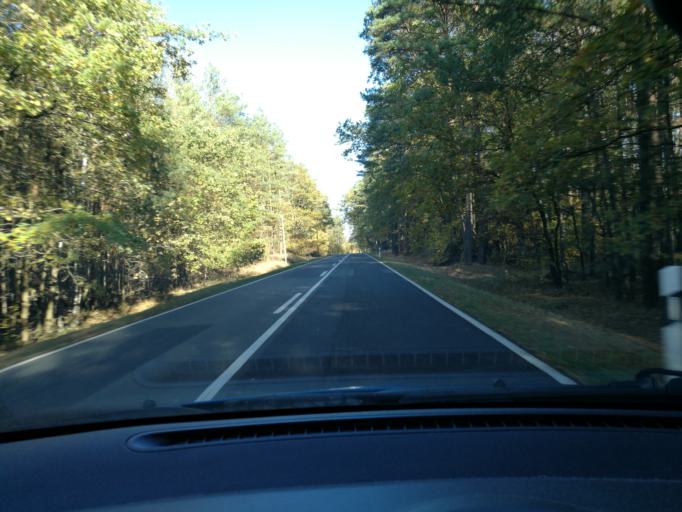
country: DE
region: Brandenburg
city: Lanz
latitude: 53.1343
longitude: 11.5580
